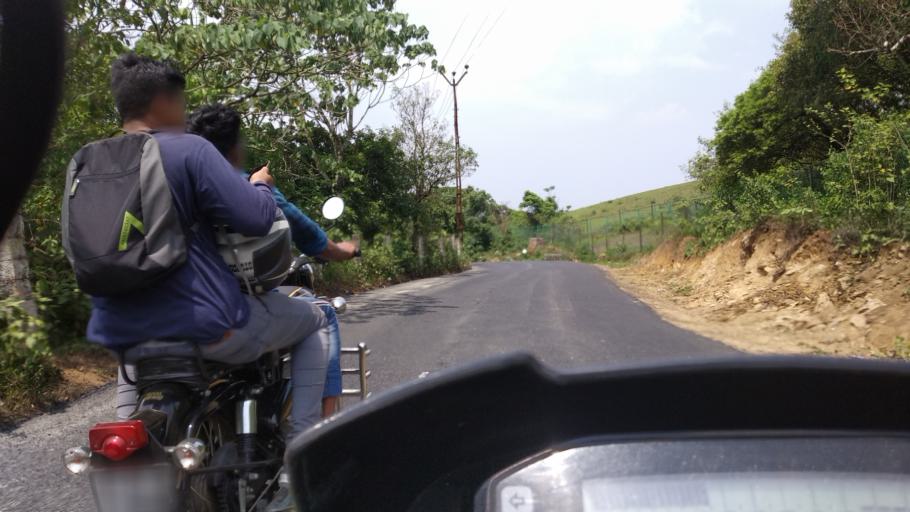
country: IN
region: Kerala
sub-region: Kottayam
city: Erattupetta
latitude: 9.6467
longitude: 76.9273
